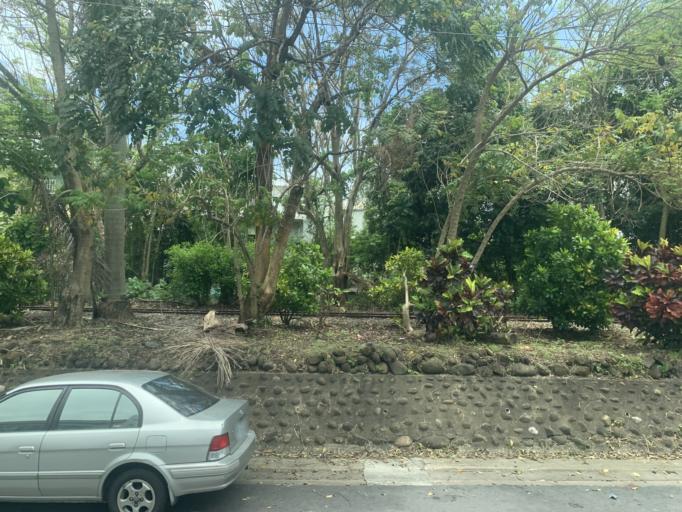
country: TW
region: Taiwan
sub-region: Chiayi
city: Jiayi Shi
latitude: 23.4913
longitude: 120.4693
